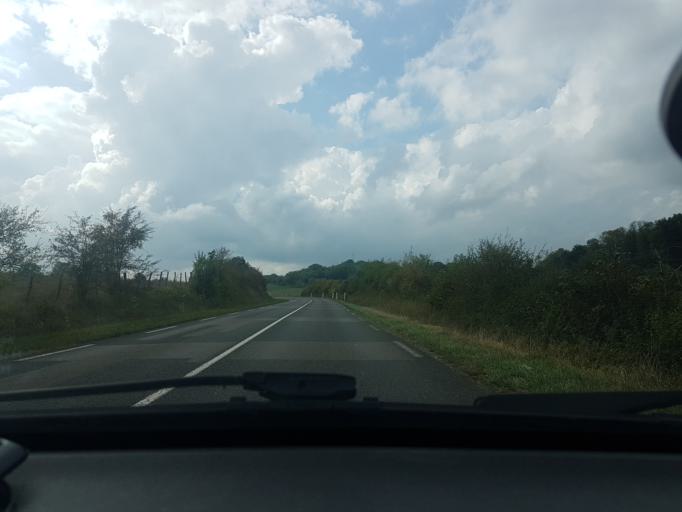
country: FR
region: Franche-Comte
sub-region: Departement du Doubs
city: Arcey
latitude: 47.5441
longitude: 6.5562
